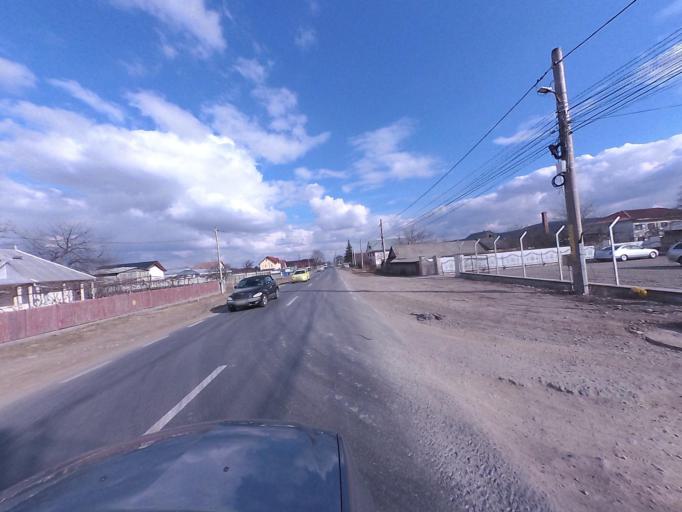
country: RO
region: Neamt
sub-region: Oras Targu Neamt
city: Targu Neamt
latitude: 47.2086
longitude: 26.3884
